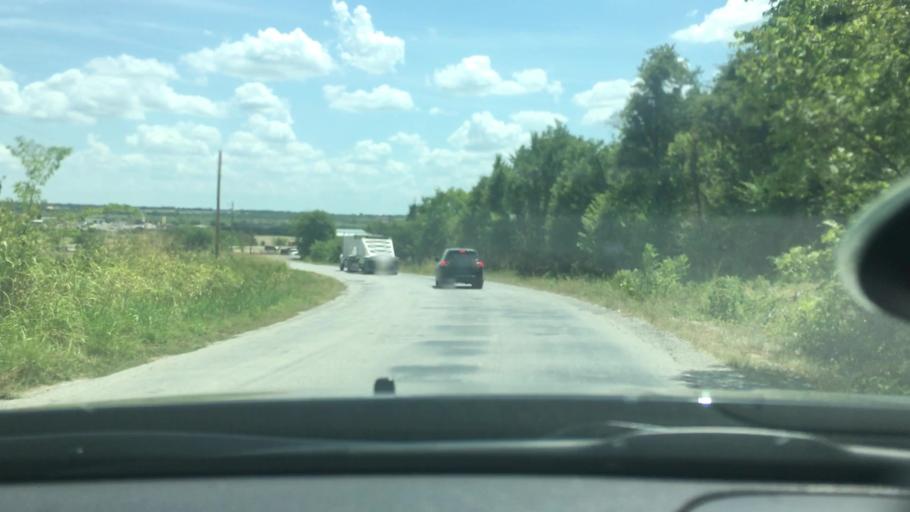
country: US
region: Oklahoma
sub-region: Carter County
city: Ardmore
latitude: 34.0785
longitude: -97.1539
